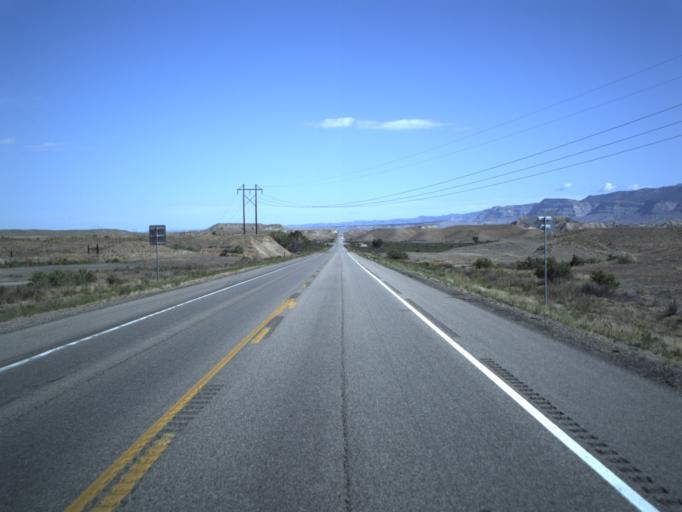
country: US
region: Utah
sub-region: Carbon County
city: East Carbon City
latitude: 39.2564
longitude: -110.3401
